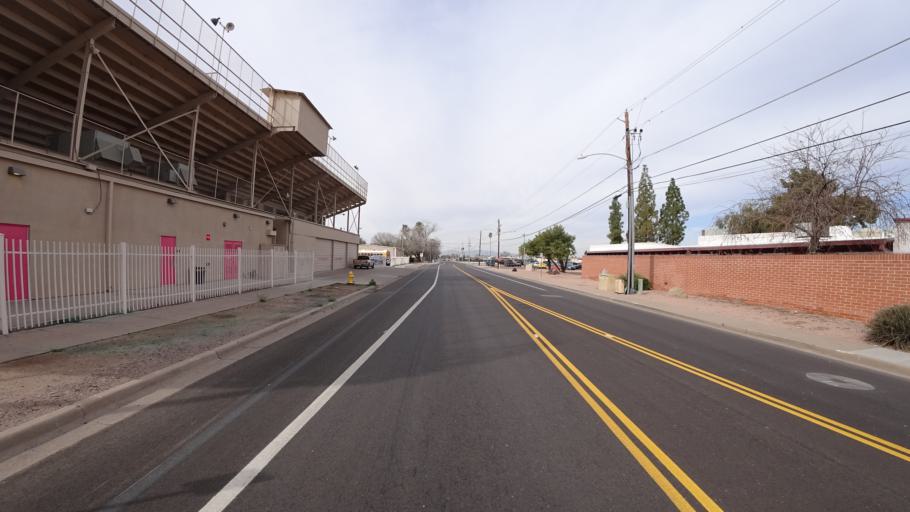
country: US
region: Arizona
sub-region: Maricopa County
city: Glendale
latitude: 33.5421
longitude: -112.1938
